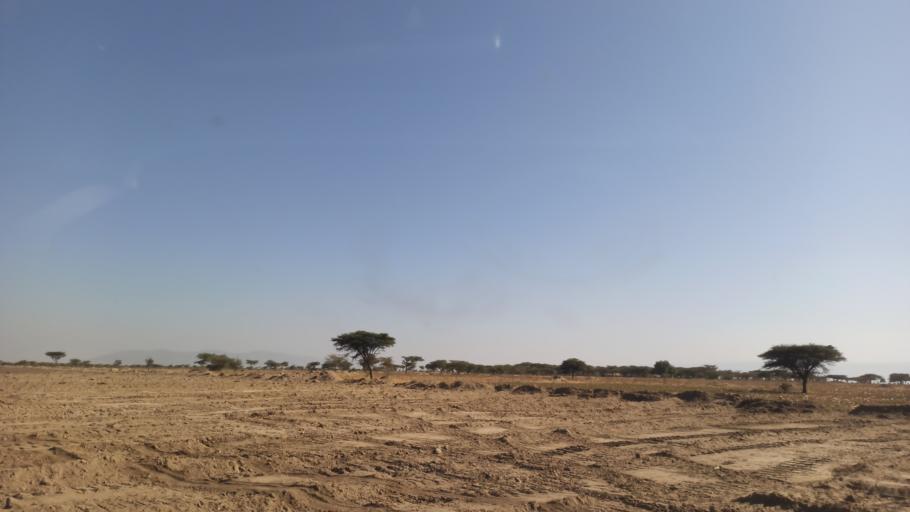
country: ET
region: Oromiya
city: Shashemene
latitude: 7.5476
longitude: 38.6728
